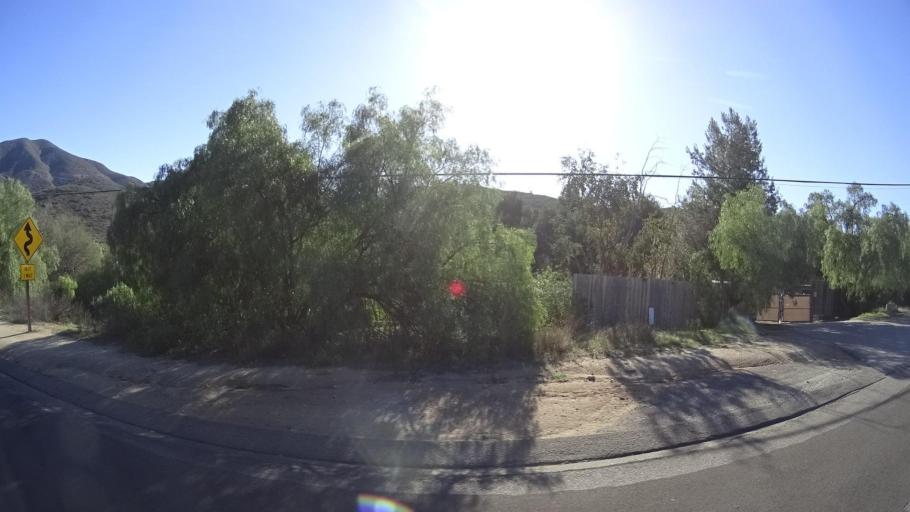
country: MX
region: Baja California
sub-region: Tijuana
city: Villa del Campo
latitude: 32.6290
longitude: -116.7647
